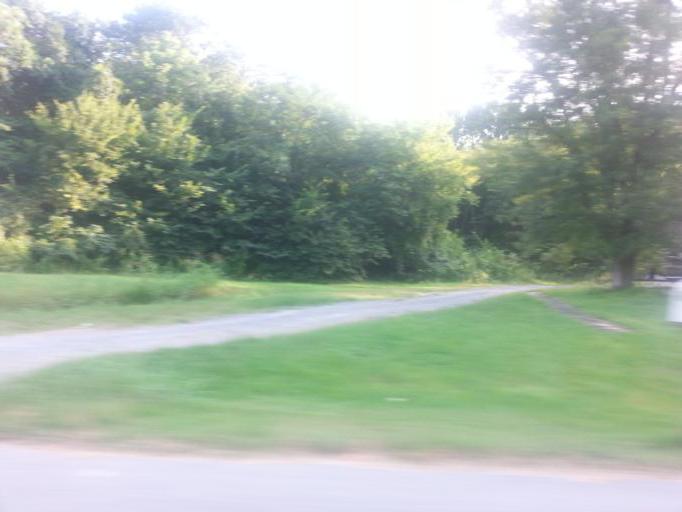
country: US
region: Tennessee
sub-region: Sevier County
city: Sevierville
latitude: 35.8732
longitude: -83.5782
